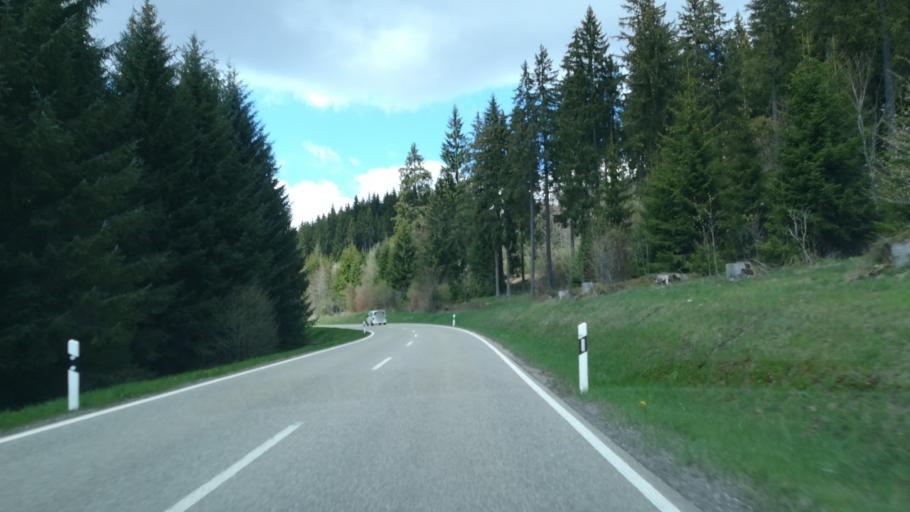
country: DE
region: Baden-Wuerttemberg
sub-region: Freiburg Region
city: Schluchsee
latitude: 47.7959
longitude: 8.2147
